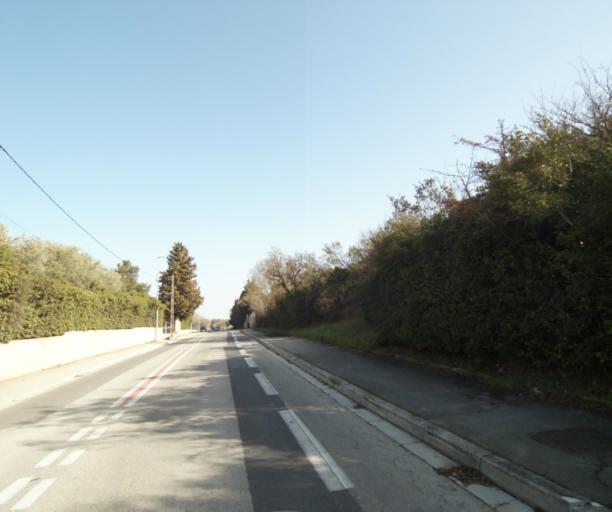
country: FR
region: Provence-Alpes-Cote d'Azur
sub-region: Departement des Bouches-du-Rhone
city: Aix-en-Provence
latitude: 43.5488
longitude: 5.4558
